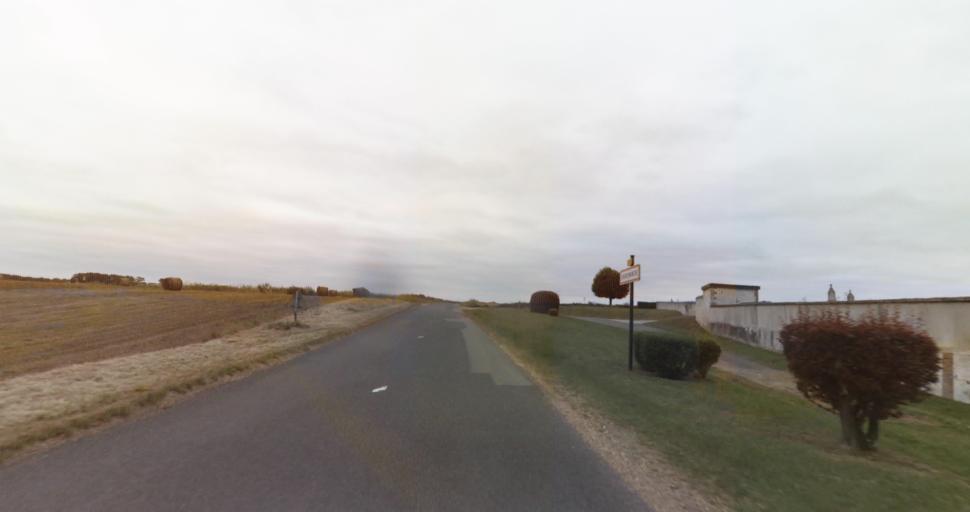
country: FR
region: Haute-Normandie
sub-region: Departement de l'Eure
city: Saint-Germain-sur-Avre
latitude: 48.8120
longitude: 1.2782
